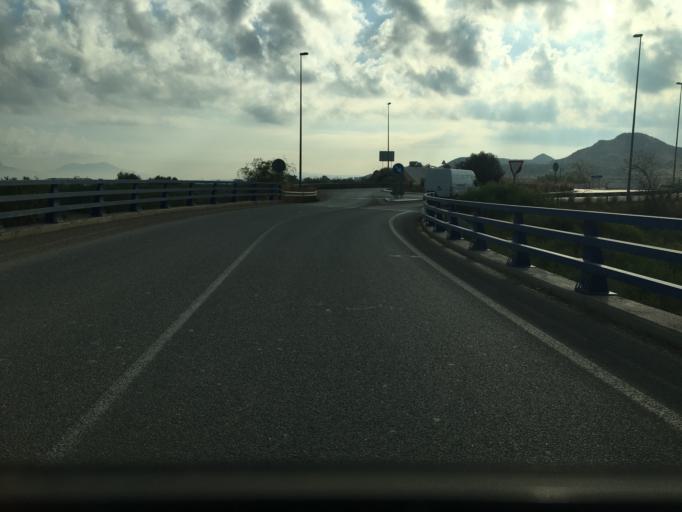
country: ES
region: Murcia
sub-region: Murcia
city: Beniel
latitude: 38.0018
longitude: -1.0153
